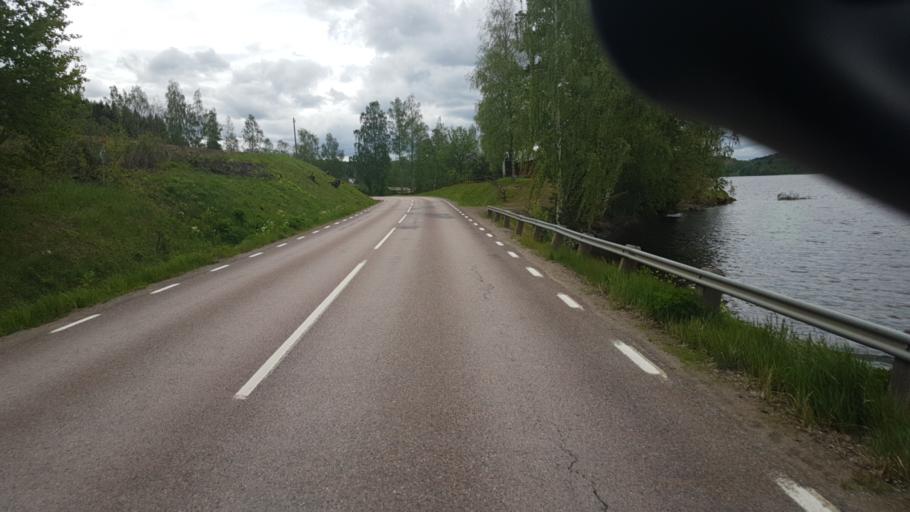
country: SE
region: Vaermland
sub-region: Arvika Kommun
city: Arvika
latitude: 59.8411
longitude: 12.5559
